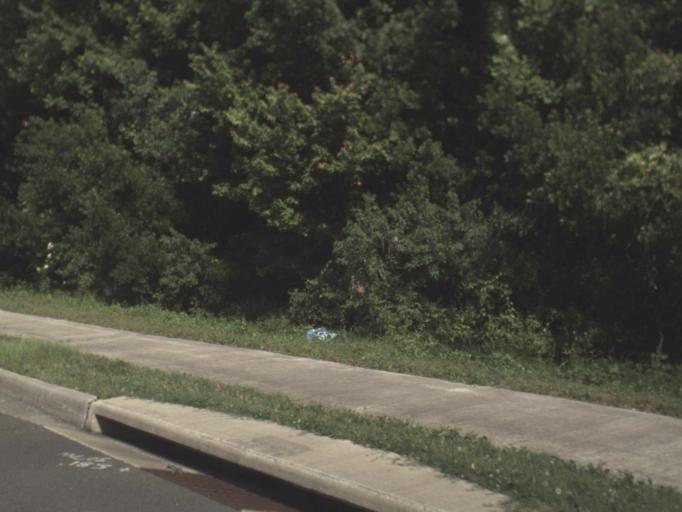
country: US
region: Florida
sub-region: Duval County
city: Atlantic Beach
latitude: 30.3540
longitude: -81.5270
